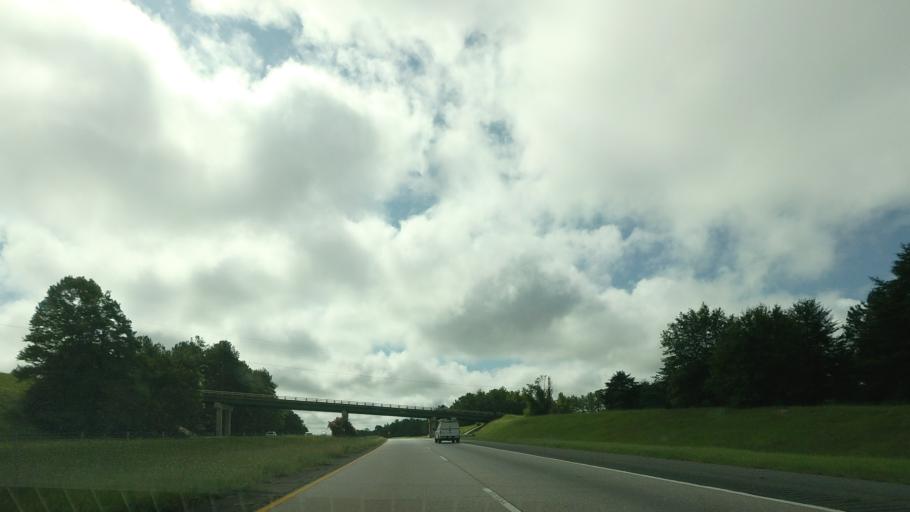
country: US
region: Georgia
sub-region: Houston County
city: Warner Robins
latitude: 32.7212
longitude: -83.5324
